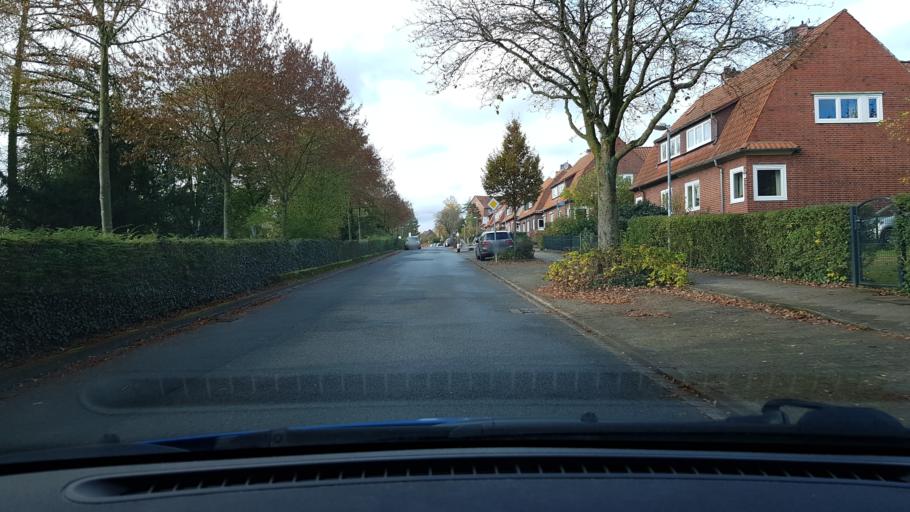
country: DE
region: Lower Saxony
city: Lueneburg
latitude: 53.2550
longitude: 10.3955
